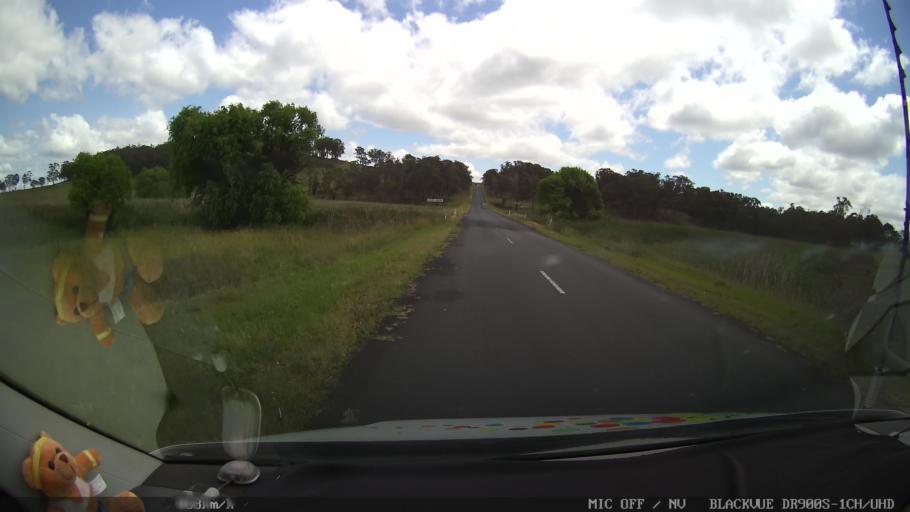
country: AU
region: New South Wales
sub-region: Glen Innes Severn
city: Glen Innes
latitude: -29.5954
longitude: 151.6664
